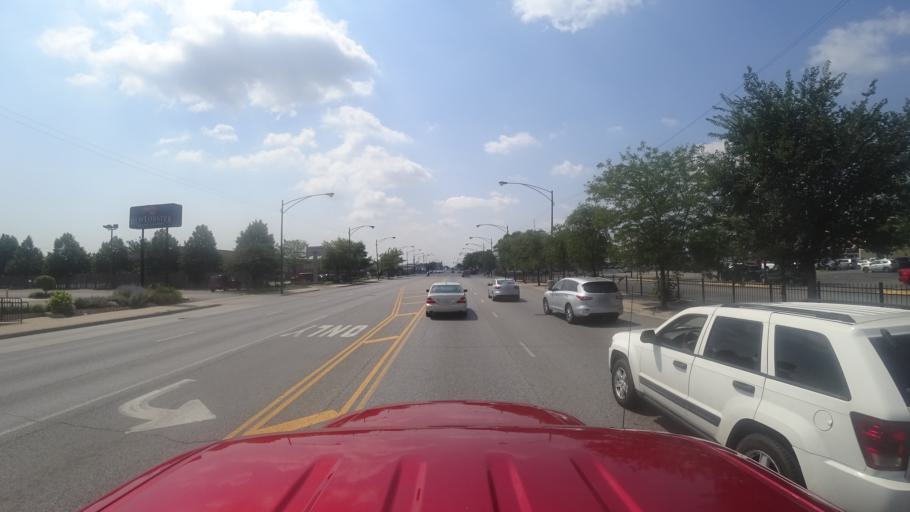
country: US
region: Illinois
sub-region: Cook County
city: Cicero
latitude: 41.7985
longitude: -87.7234
